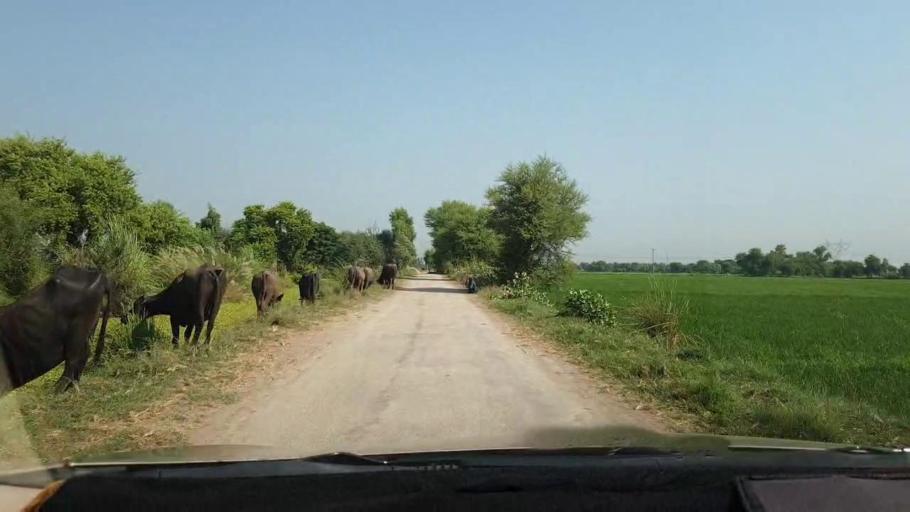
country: PK
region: Sindh
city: Larkana
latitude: 27.6351
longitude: 68.2371
